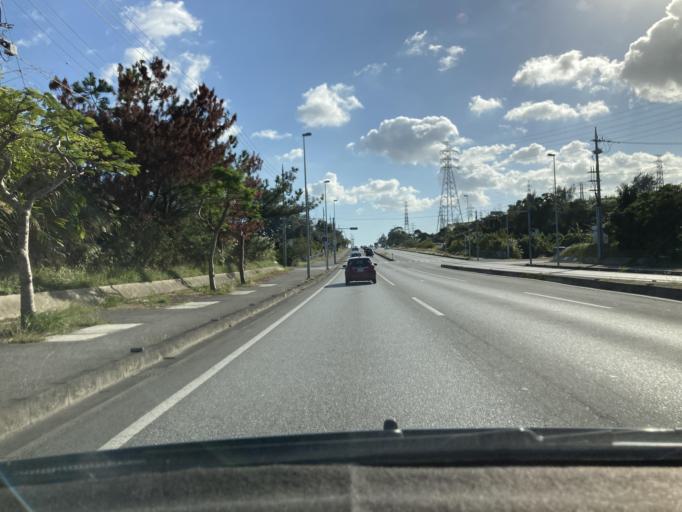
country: JP
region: Okinawa
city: Ishikawa
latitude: 26.3971
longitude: 127.8289
